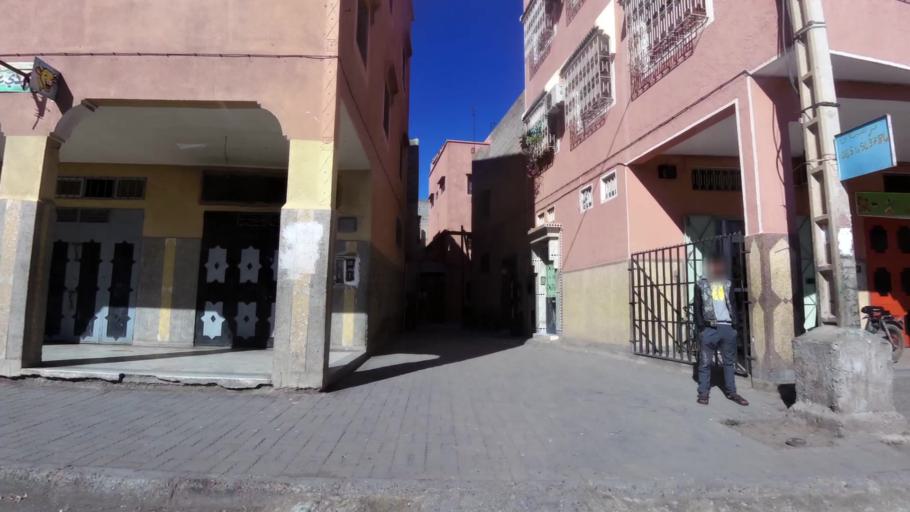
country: MA
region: Marrakech-Tensift-Al Haouz
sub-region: Marrakech
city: Marrakesh
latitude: 31.5917
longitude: -8.0346
